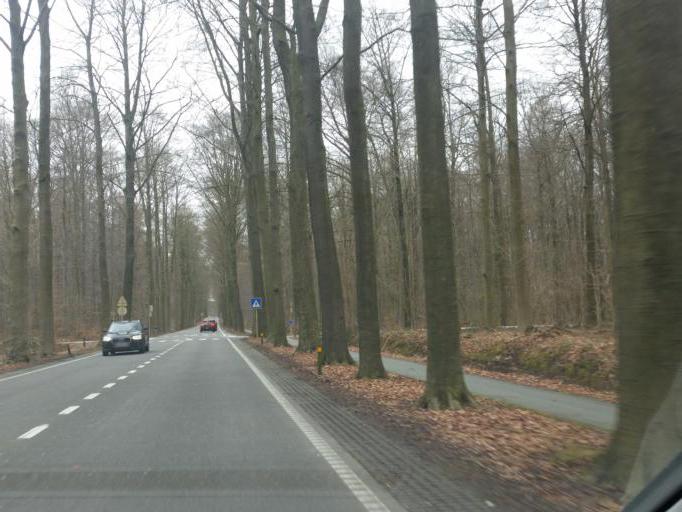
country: BE
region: Flanders
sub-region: Provincie Vlaams-Brabant
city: Sint-Genesius-Rode
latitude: 50.7777
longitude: 4.3893
